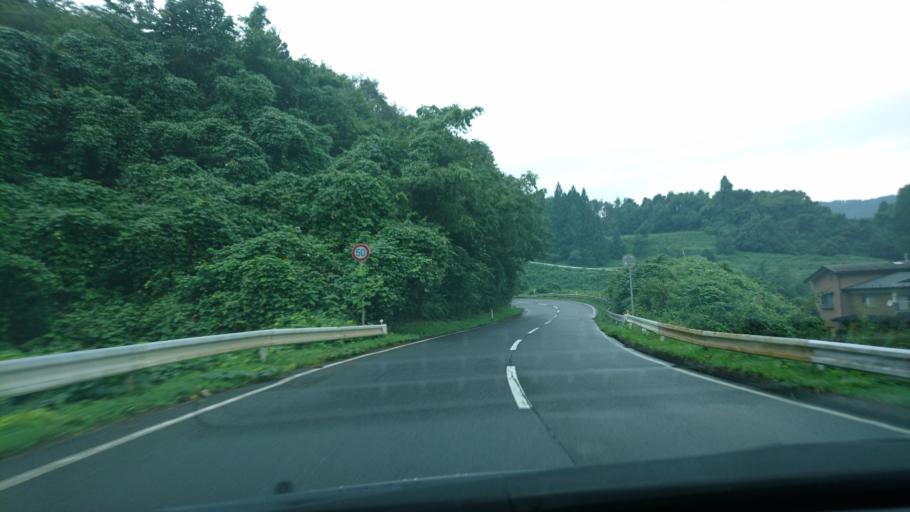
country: JP
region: Iwate
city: Ichinoseki
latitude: 39.0176
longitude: 141.2193
